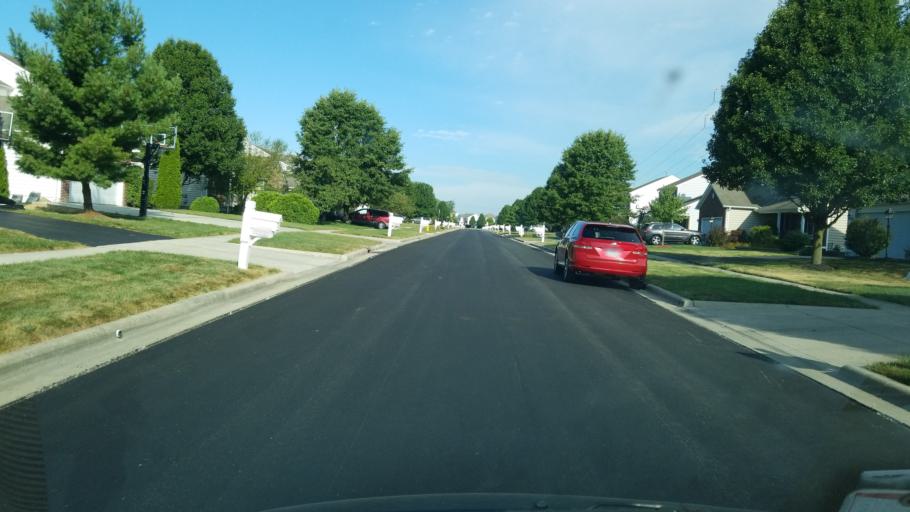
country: US
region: Ohio
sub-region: Delaware County
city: Lewis Center
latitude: 40.1760
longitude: -83.0019
